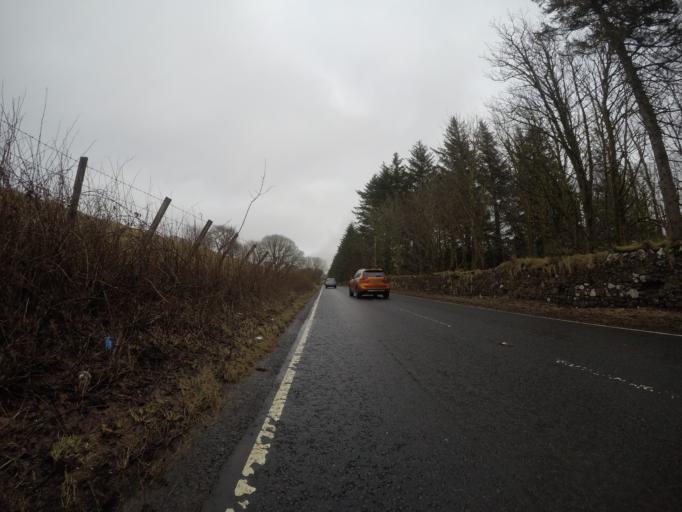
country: GB
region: Scotland
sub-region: North Ayrshire
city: Fairlie
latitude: 55.7751
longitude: -4.8321
